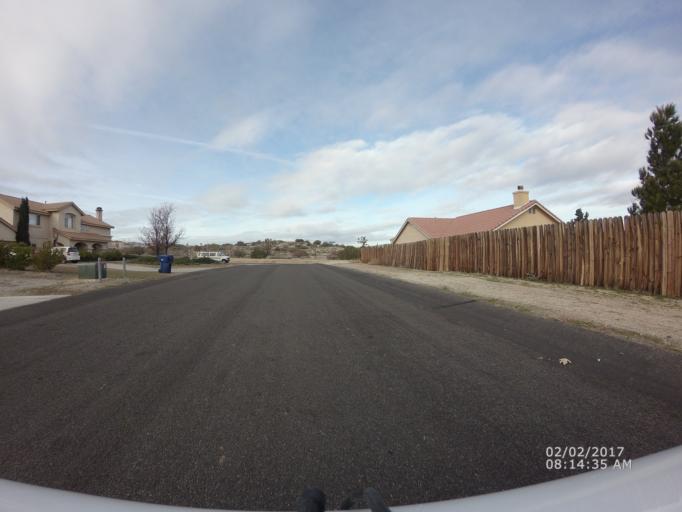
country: US
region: California
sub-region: Los Angeles County
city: Littlerock
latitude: 34.5315
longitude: -118.0358
